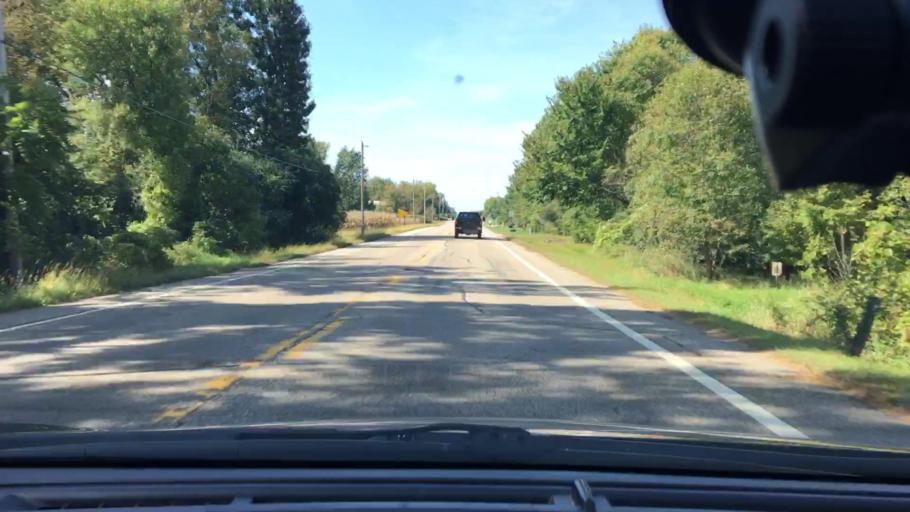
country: US
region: Minnesota
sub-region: Wright County
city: Hanover
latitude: 45.1236
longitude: -93.6291
